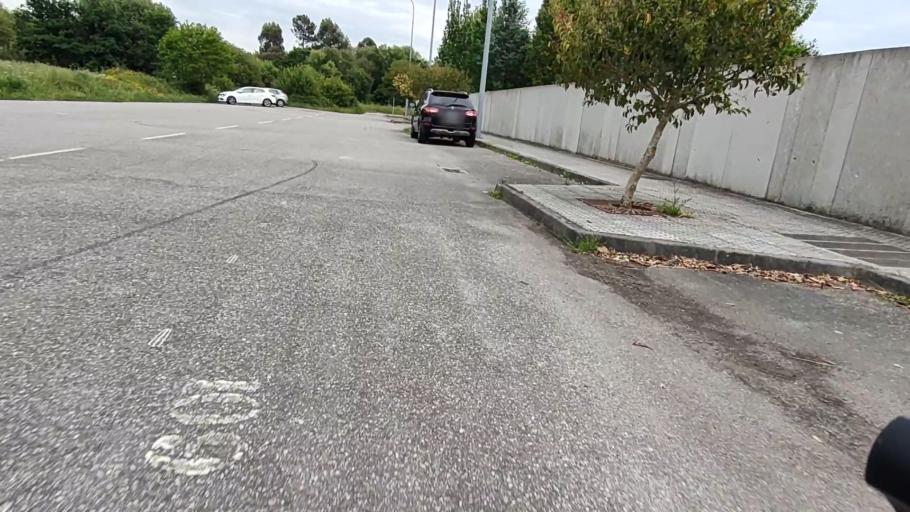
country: ES
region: Galicia
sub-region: Provincia da Coruna
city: Boiro
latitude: 42.6416
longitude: -8.8857
